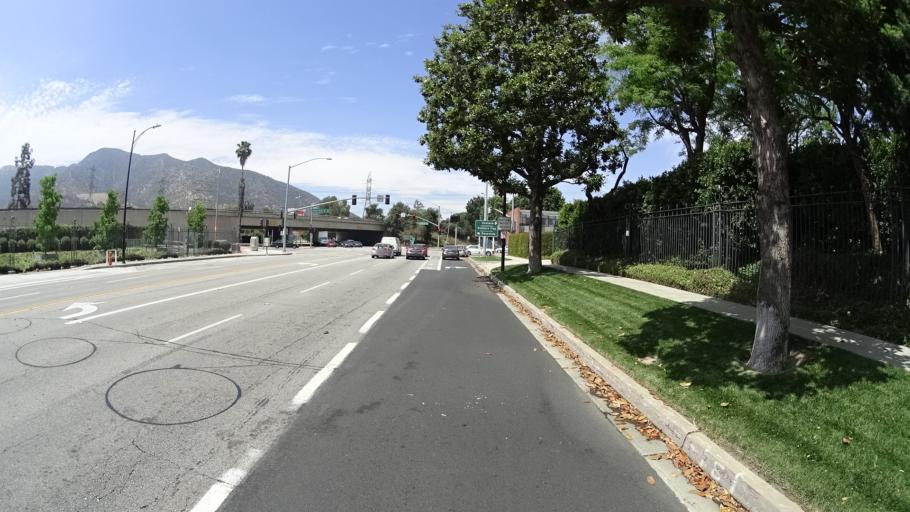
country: US
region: California
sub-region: Los Angeles County
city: Burbank
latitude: 34.1546
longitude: -118.3255
